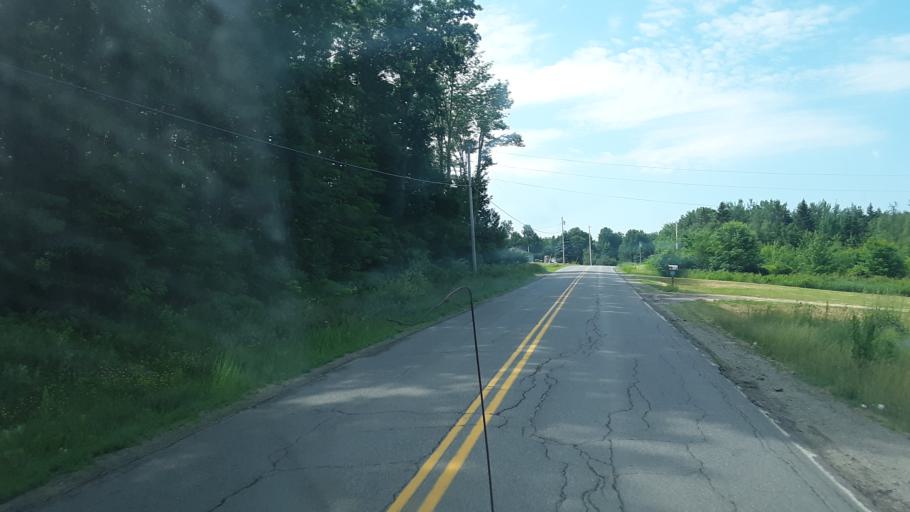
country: US
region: Maine
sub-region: Waldo County
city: Frankfort
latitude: 44.5890
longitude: -68.9441
